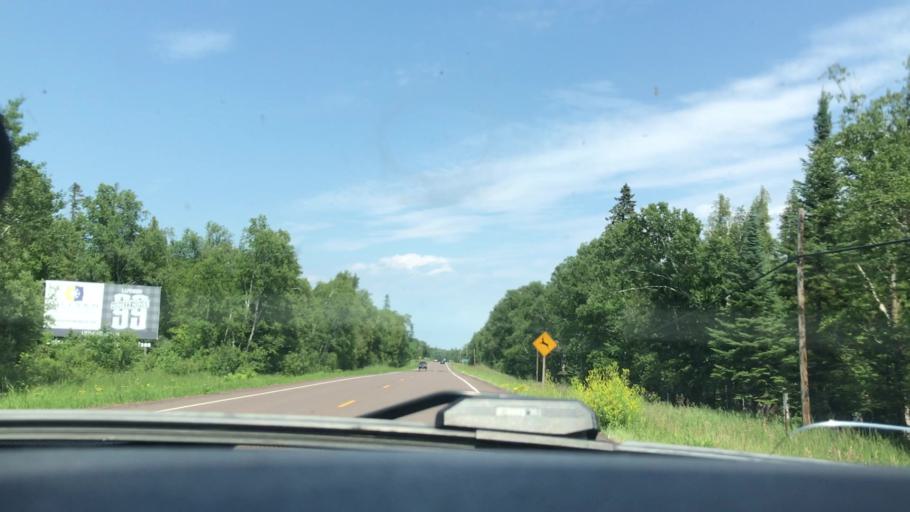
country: US
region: Minnesota
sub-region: Cook County
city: Grand Marais
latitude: 47.6347
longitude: -90.7172
